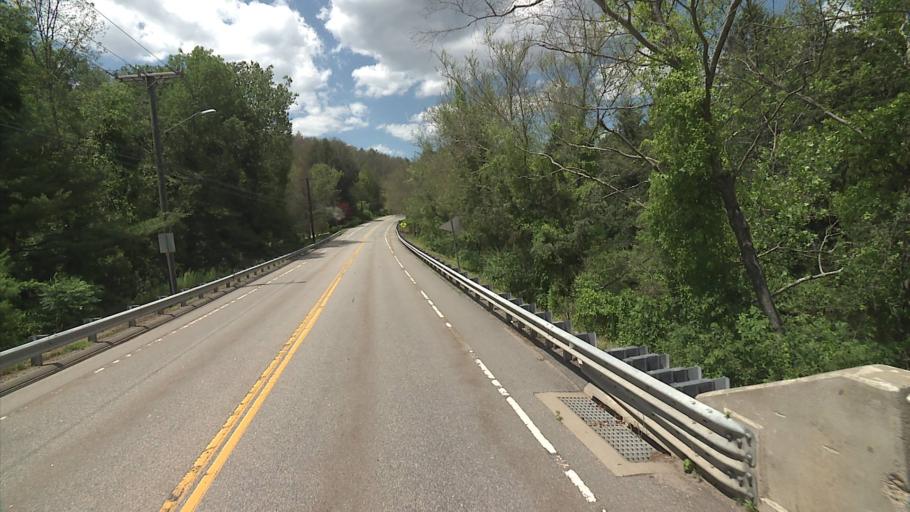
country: US
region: Connecticut
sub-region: Middlesex County
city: Moodus
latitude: 41.5134
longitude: -72.4826
